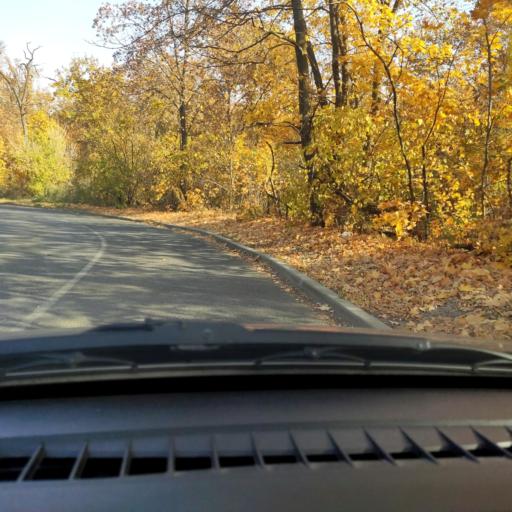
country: RU
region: Samara
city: Tol'yatti
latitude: 53.5207
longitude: 49.3311
